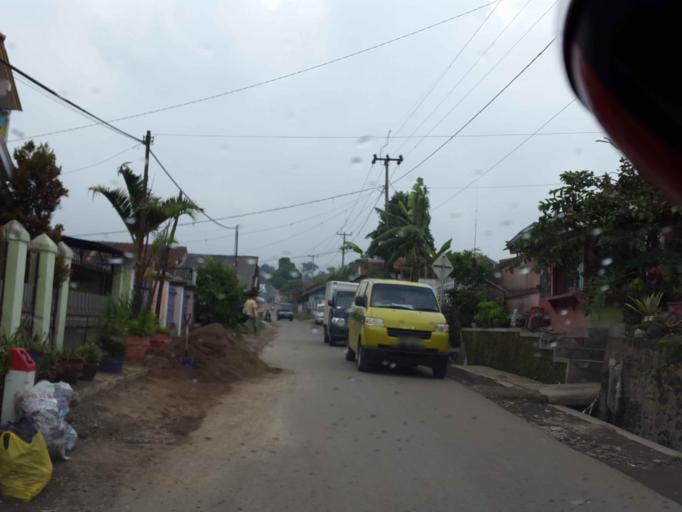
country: ID
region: West Java
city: Lembang
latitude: -6.8123
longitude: 107.5767
